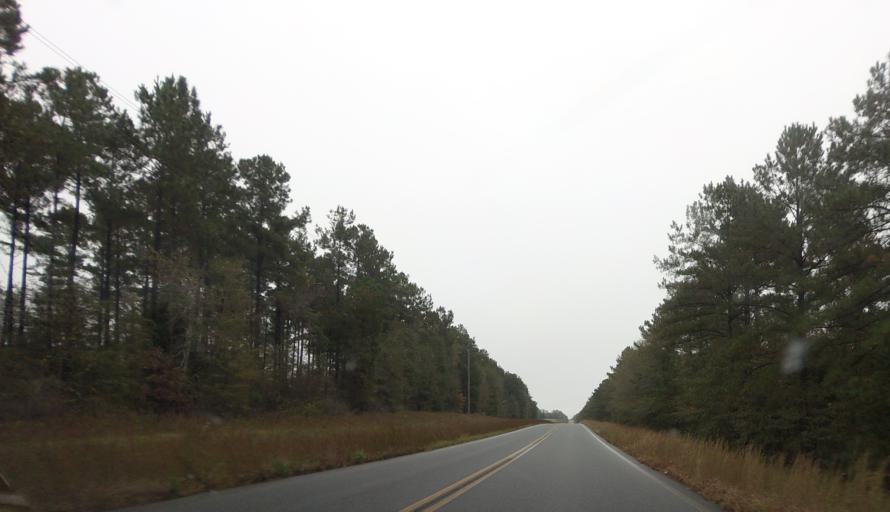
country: US
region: Georgia
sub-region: Marion County
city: Buena Vista
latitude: 32.3982
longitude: -84.4193
